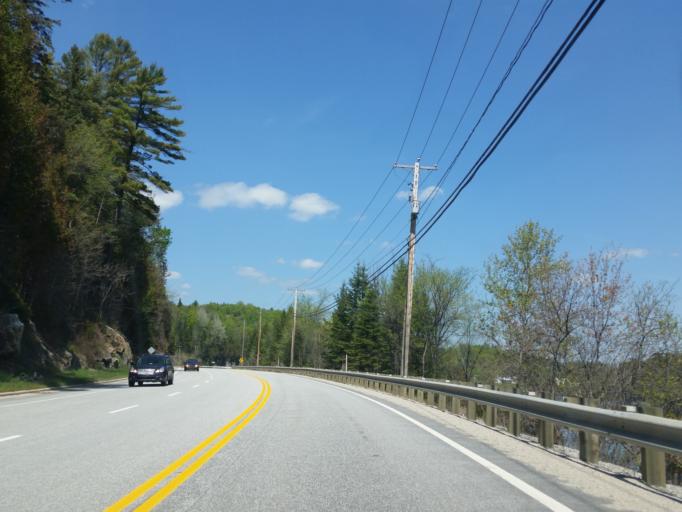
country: CA
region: Quebec
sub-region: Outaouais
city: Wakefield
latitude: 45.6754
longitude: -75.9292
